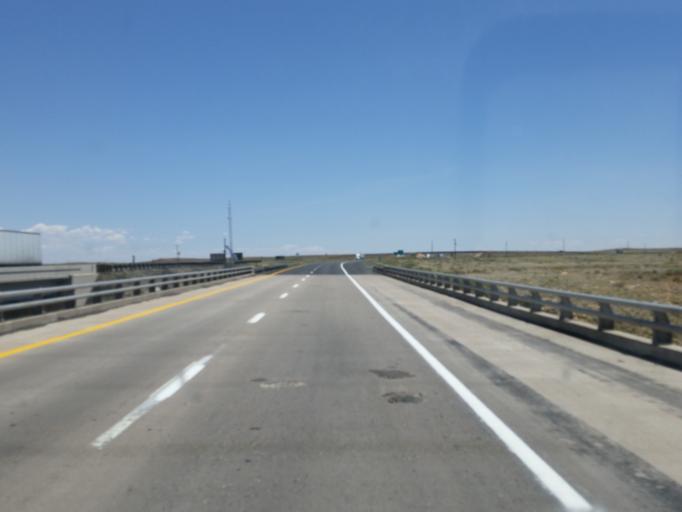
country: US
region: Arizona
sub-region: Coconino County
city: LeChee
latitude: 35.1174
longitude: -111.1001
